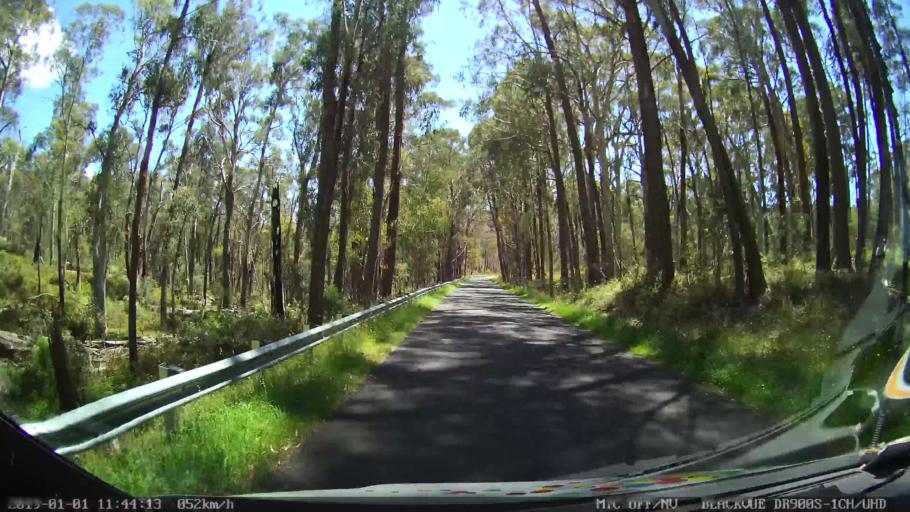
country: AU
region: New South Wales
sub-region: Snowy River
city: Jindabyne
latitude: -35.9016
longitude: 148.3910
